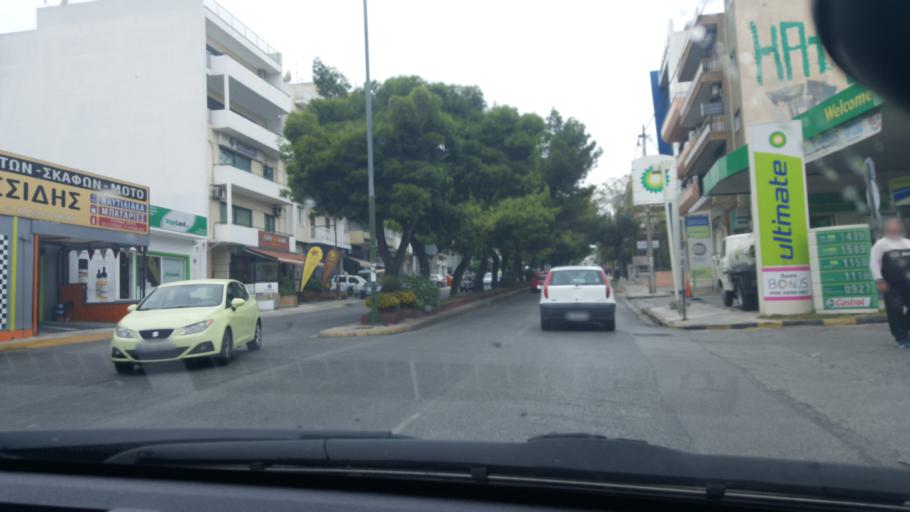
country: GR
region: Attica
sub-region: Nomarchia Athinas
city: Neo Psychiko
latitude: 37.9937
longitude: 23.7752
